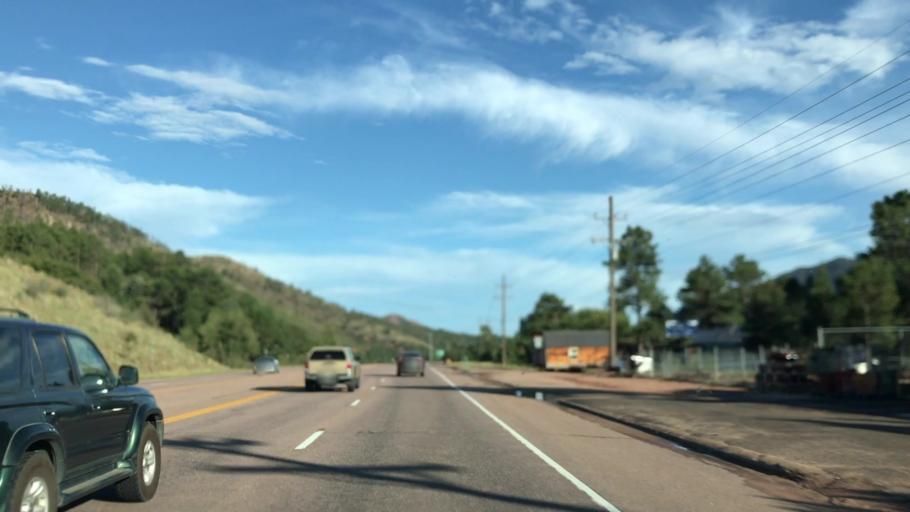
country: US
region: Colorado
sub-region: El Paso County
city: Cascade-Chipita Park
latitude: 38.9150
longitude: -104.9805
